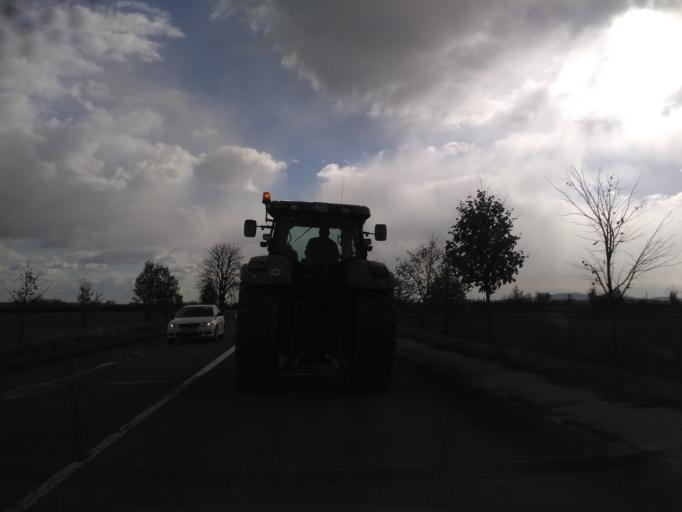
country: SK
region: Kosicky
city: Trebisov
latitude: 48.6411
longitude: 21.6835
